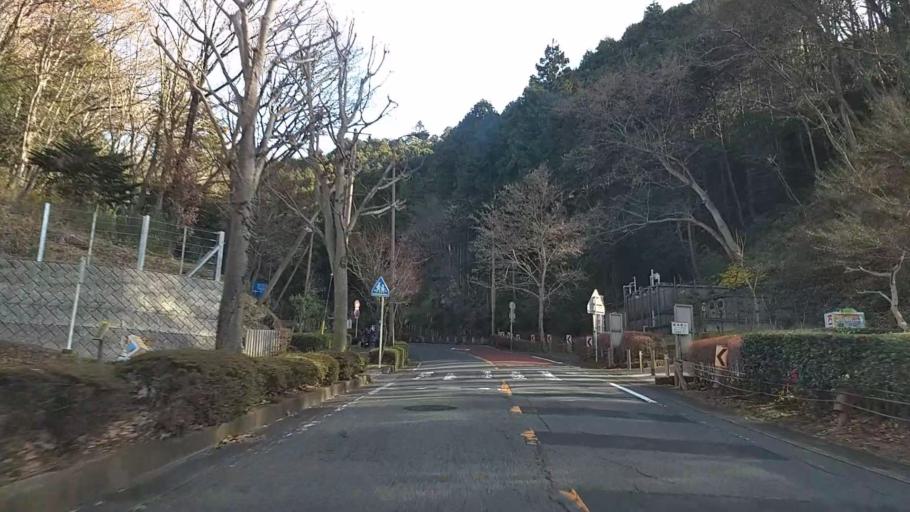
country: JP
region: Kanagawa
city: Isehara
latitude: 35.4466
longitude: 139.3005
